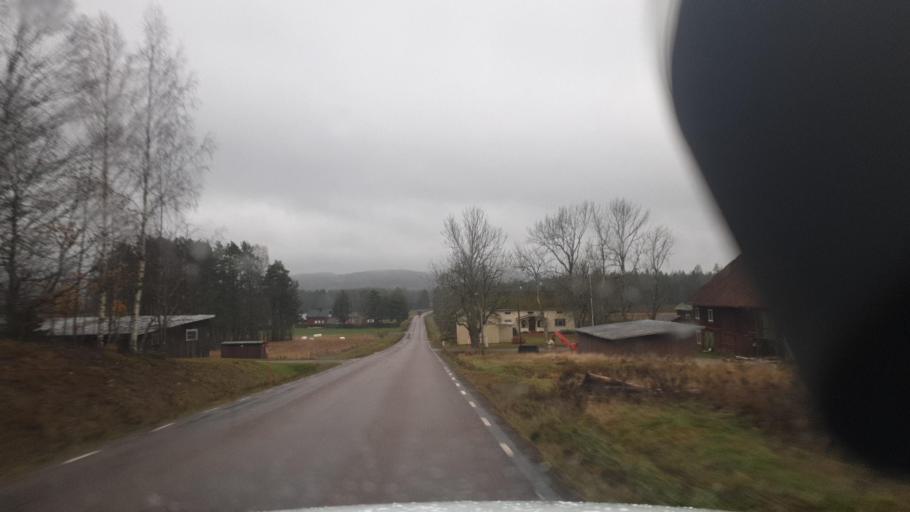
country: SE
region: Vaermland
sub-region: Eda Kommun
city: Charlottenberg
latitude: 59.7428
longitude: 12.1669
